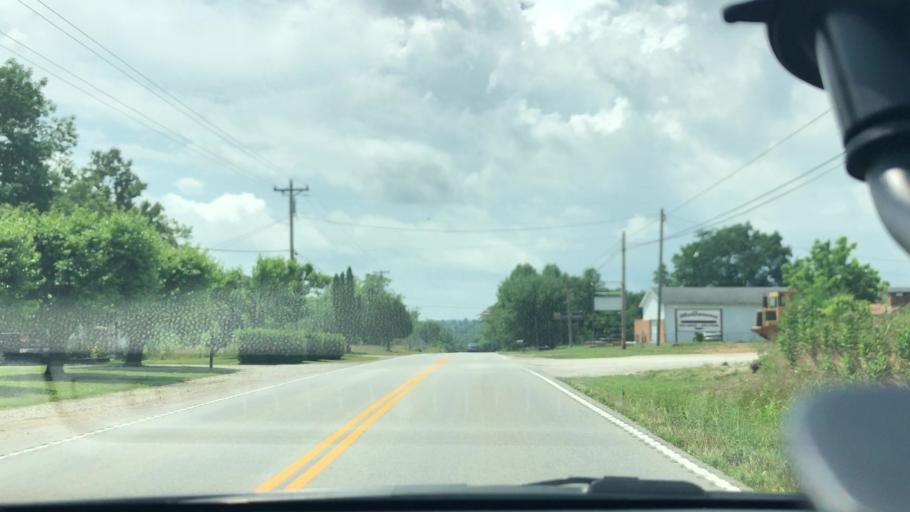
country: US
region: Kentucky
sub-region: Pulaski County
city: Somerset
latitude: 37.0595
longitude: -84.6757
